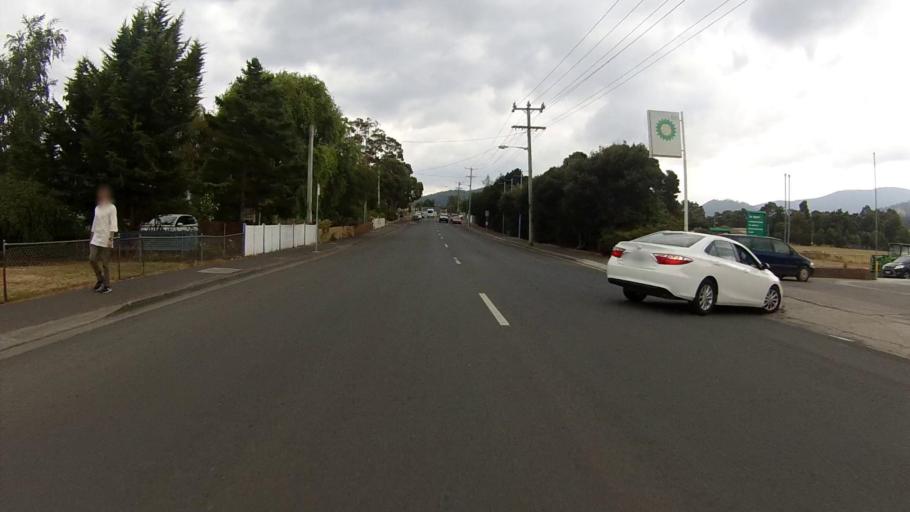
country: AU
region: Tasmania
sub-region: Huon Valley
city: Cygnet
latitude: -43.1600
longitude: 147.0757
